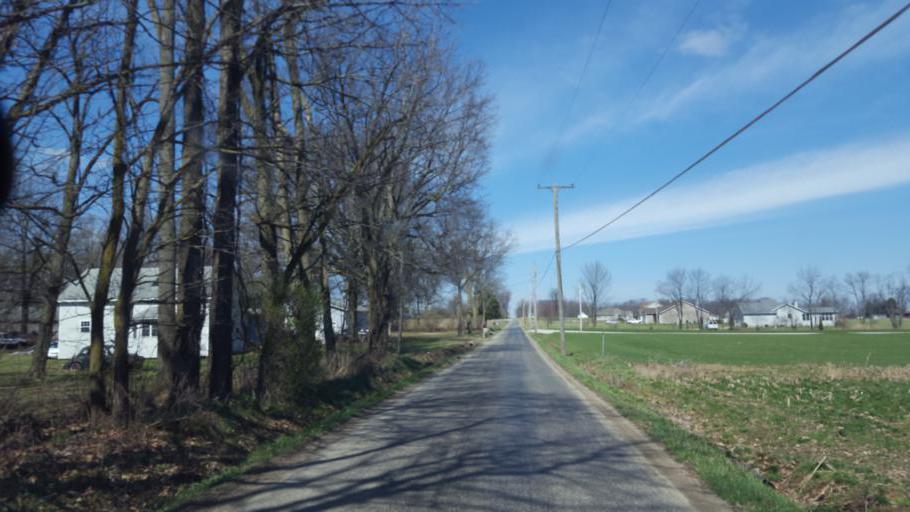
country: US
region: Ohio
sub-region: Ashland County
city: Ashland
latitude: 40.8864
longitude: -82.3585
